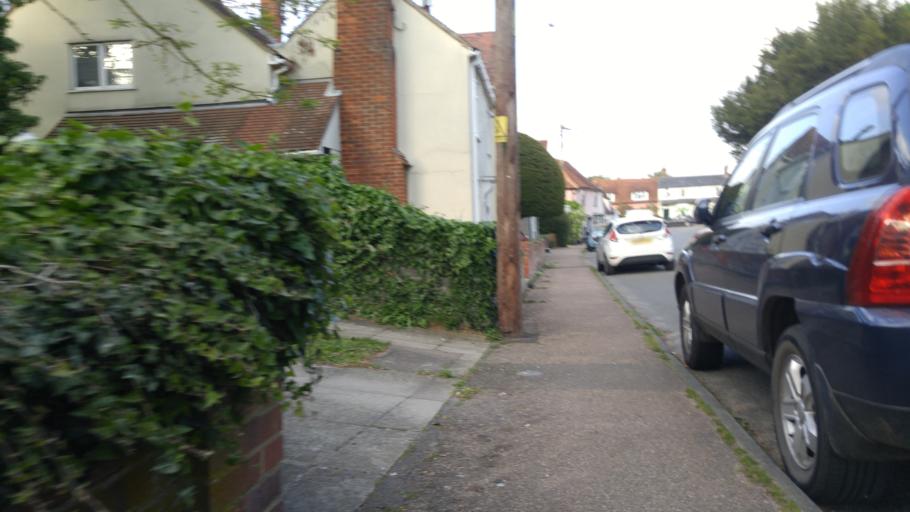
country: GB
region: England
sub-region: Essex
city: Tiptree
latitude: 51.8370
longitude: 0.7515
